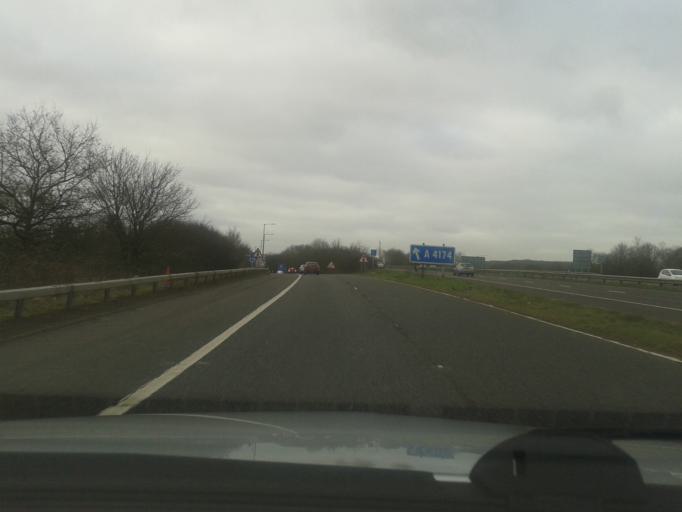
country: GB
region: England
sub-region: South Gloucestershire
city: Stoke Gifford
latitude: 51.5079
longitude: -2.5254
